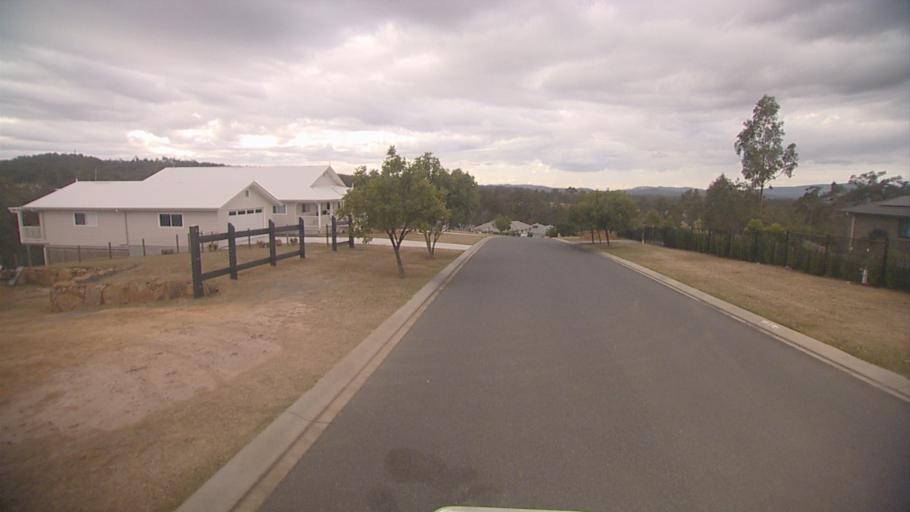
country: AU
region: Queensland
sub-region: Logan
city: Cedar Vale
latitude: -27.8641
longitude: 153.0766
